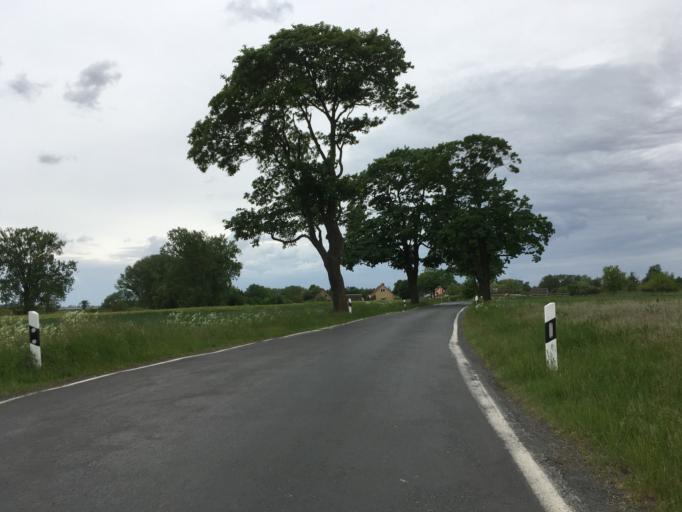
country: DE
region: Brandenburg
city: Werneuchen
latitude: 52.6670
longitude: 13.6943
